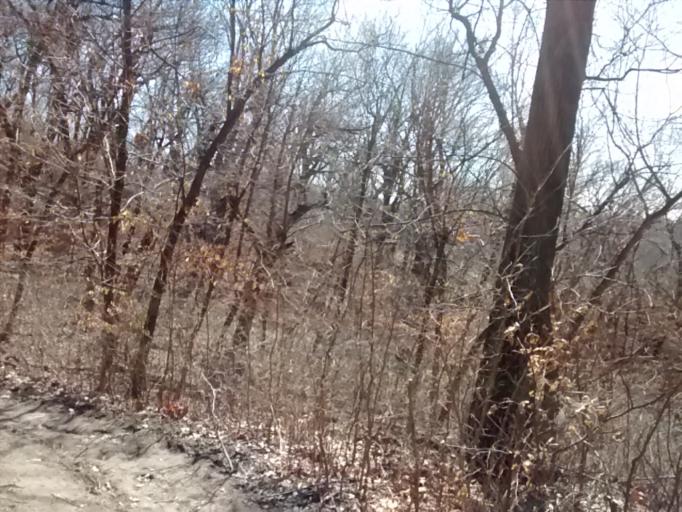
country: US
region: Nebraska
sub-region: Sarpy County
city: Bellevue
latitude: 41.1815
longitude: -95.9099
